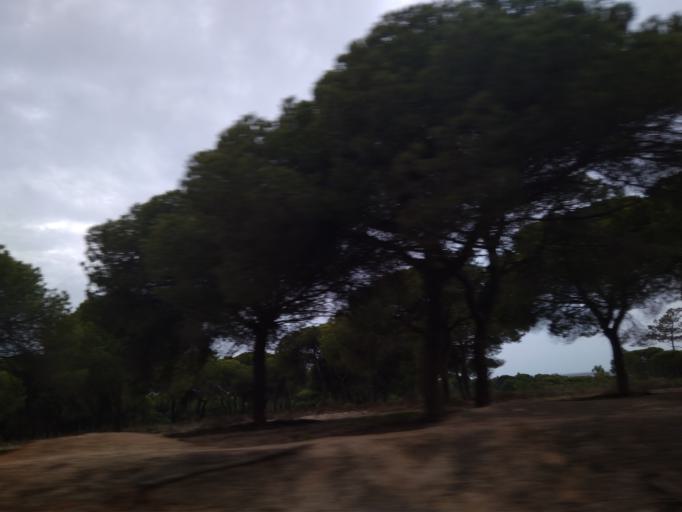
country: PT
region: Faro
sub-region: Faro
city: Faro
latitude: 37.0298
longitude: -7.9754
